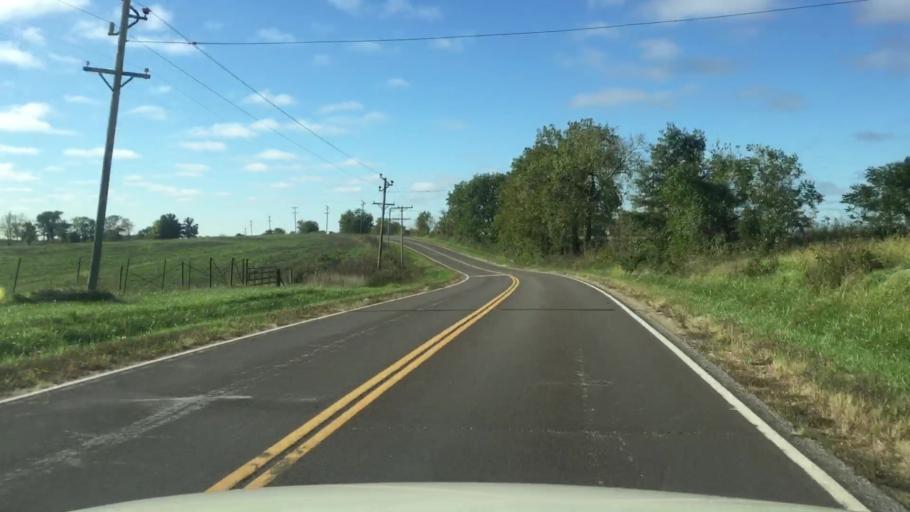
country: US
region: Missouri
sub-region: Howard County
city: New Franklin
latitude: 39.0867
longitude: -92.7449
